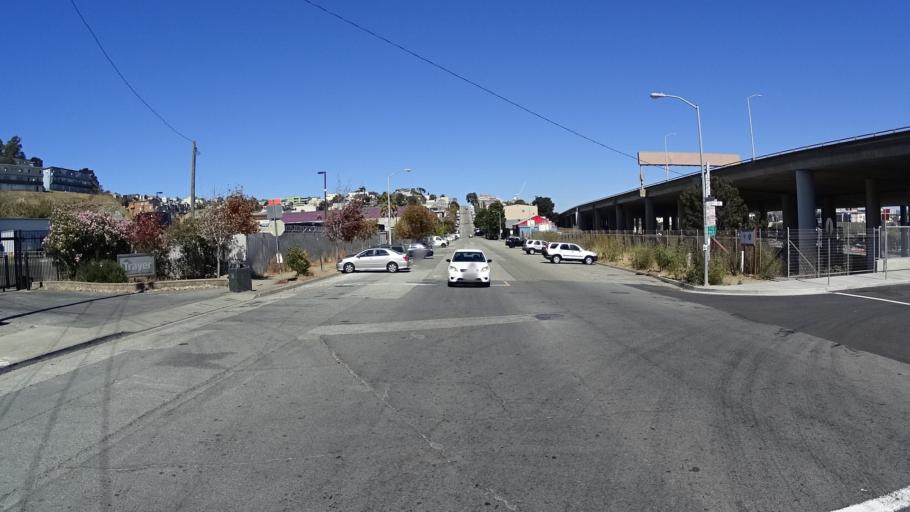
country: US
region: California
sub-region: San Francisco County
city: San Francisco
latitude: 37.7550
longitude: -122.3929
